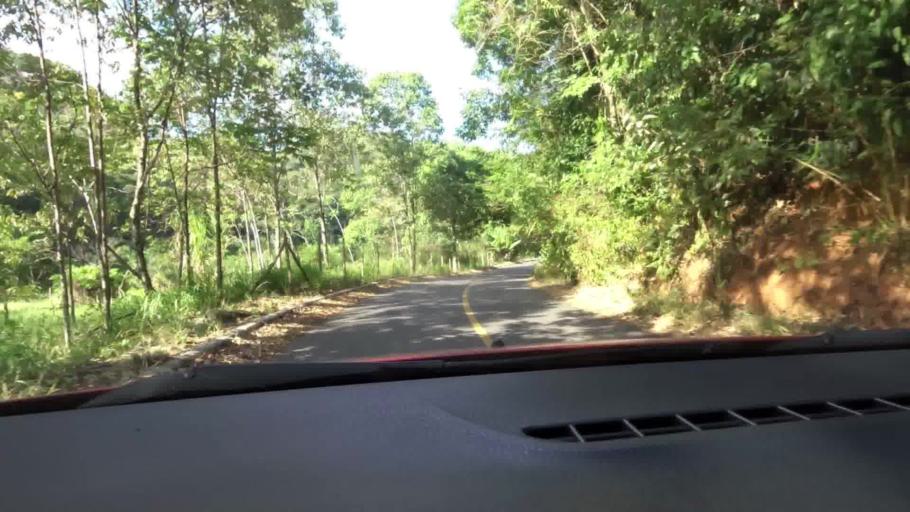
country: BR
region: Espirito Santo
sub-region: Guarapari
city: Guarapari
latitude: -20.5794
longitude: -40.5437
